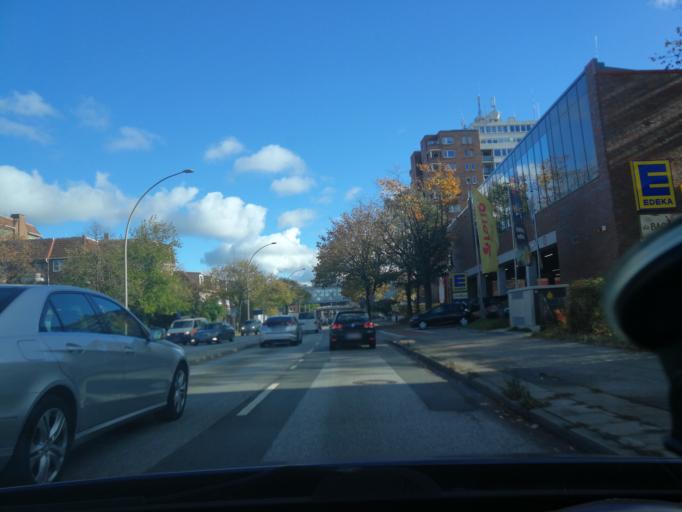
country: DE
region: Lower Saxony
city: Neu Wulmstorf
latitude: 53.4726
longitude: 9.8505
